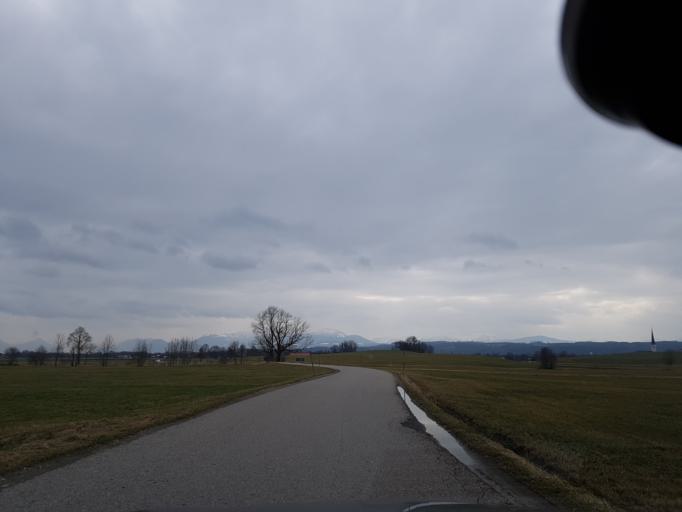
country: DE
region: Bavaria
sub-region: Upper Bavaria
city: Bruckmuhl
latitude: 47.9027
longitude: 11.9216
